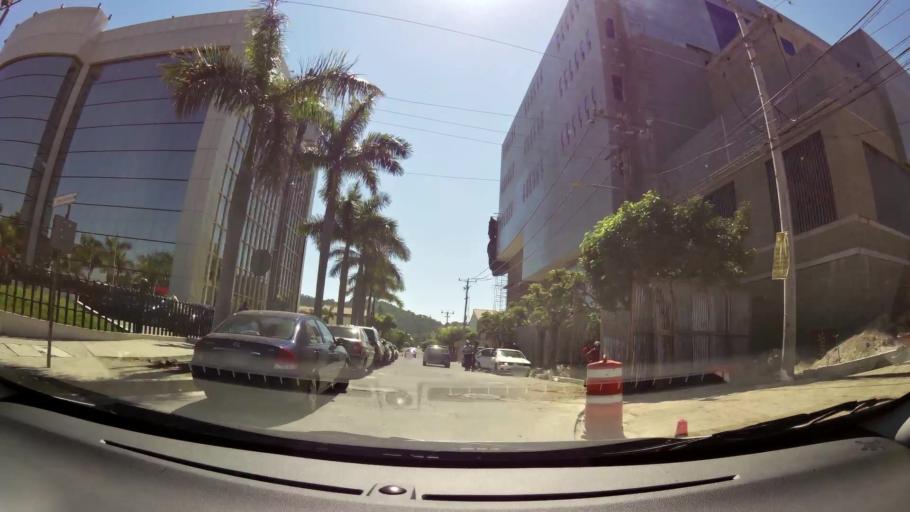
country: SV
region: La Libertad
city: Santa Tecla
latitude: 13.6715
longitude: -89.2762
